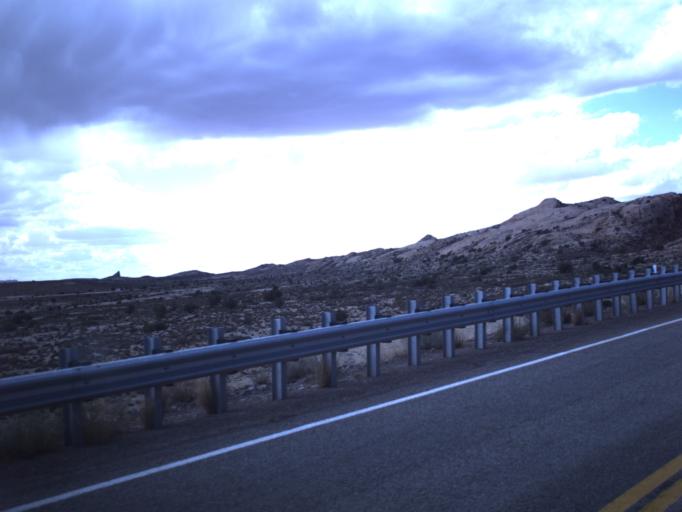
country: US
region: Utah
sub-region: San Juan County
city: Blanding
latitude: 37.2597
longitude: -109.6680
